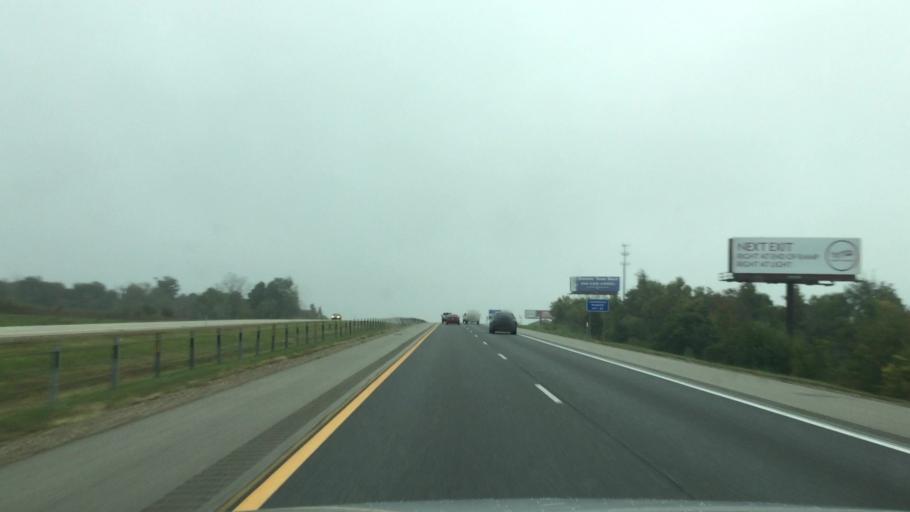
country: US
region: Michigan
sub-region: Berrien County
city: Watervliet
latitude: 42.1775
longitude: -86.2728
